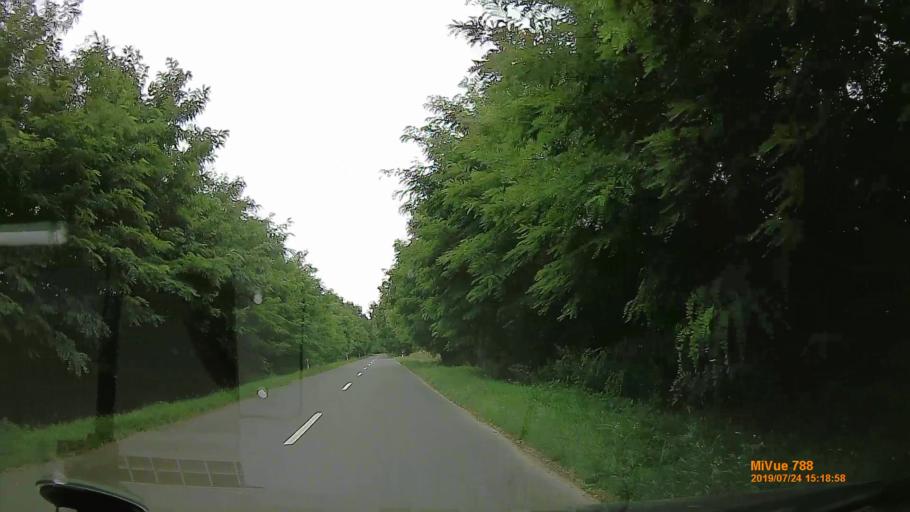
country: HU
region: Szabolcs-Szatmar-Bereg
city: Tarpa
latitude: 48.1752
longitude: 22.5454
